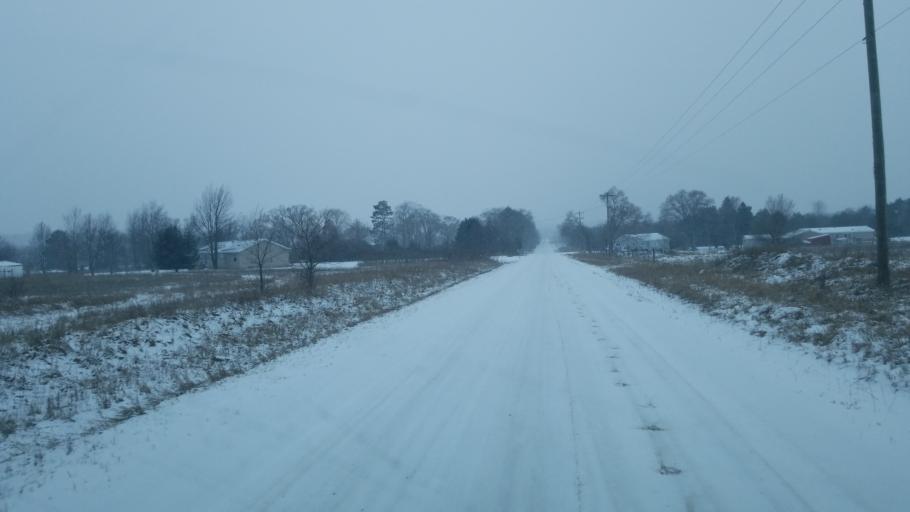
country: US
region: Michigan
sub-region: Osceola County
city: Reed City
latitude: 43.8290
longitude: -85.4113
